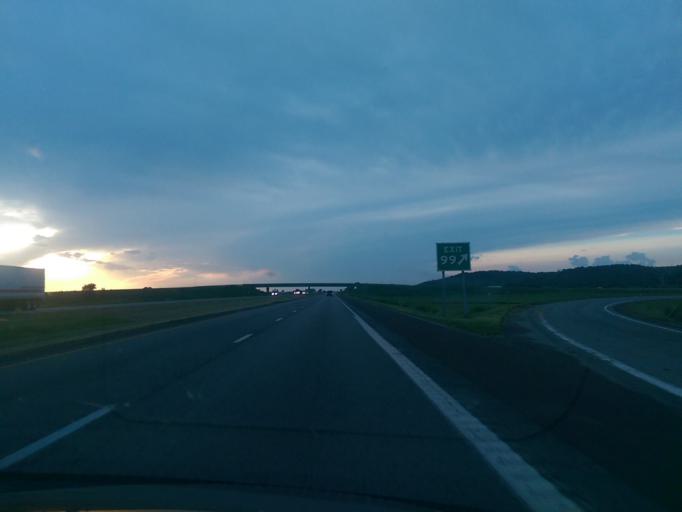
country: US
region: Missouri
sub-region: Atchison County
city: Rock Port
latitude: 40.2610
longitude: -95.4516
